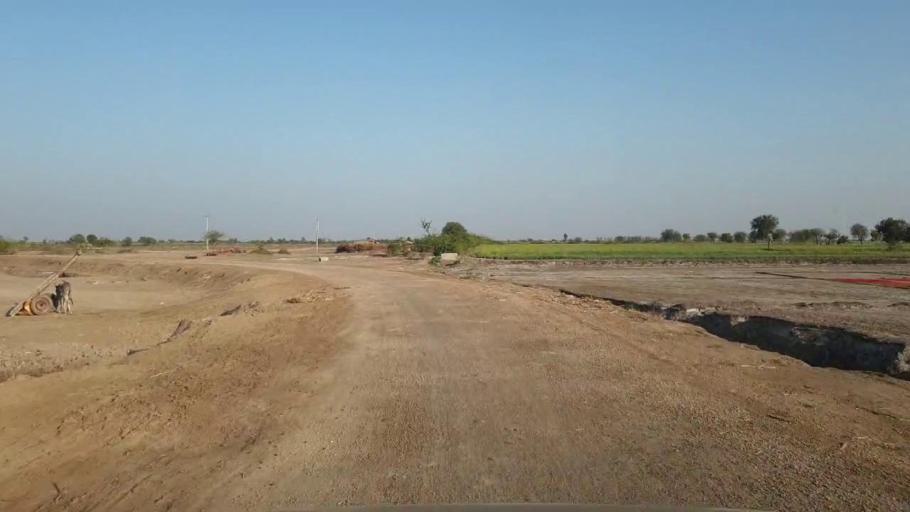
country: PK
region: Sindh
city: Samaro
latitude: 25.1386
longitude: 69.3052
